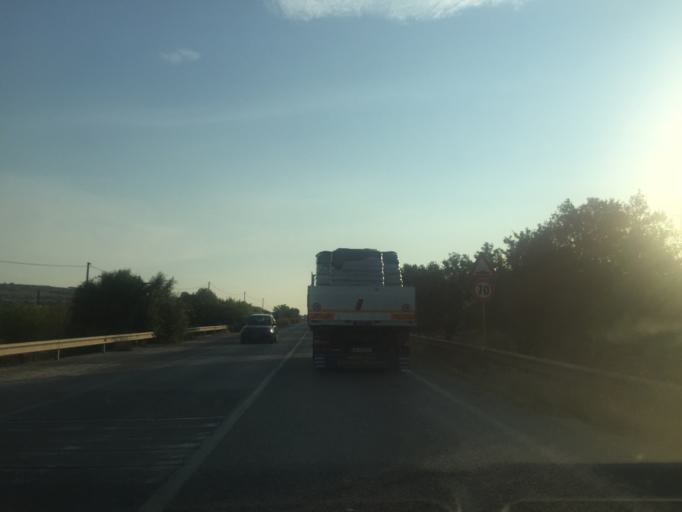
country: IT
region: Sicily
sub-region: Ragusa
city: Ispica
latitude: 36.7633
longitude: 14.8982
